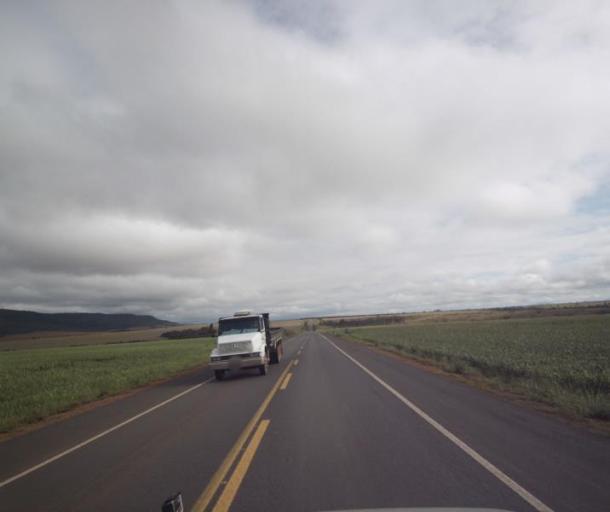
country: BR
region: Goias
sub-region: Padre Bernardo
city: Padre Bernardo
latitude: -15.4025
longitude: -48.6317
